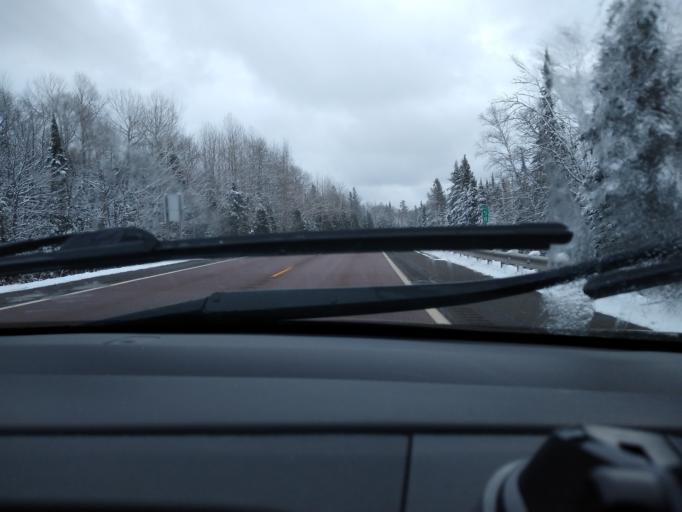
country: US
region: Wisconsin
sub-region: Vilas County
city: Eagle River
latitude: 46.2460
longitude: -89.1000
